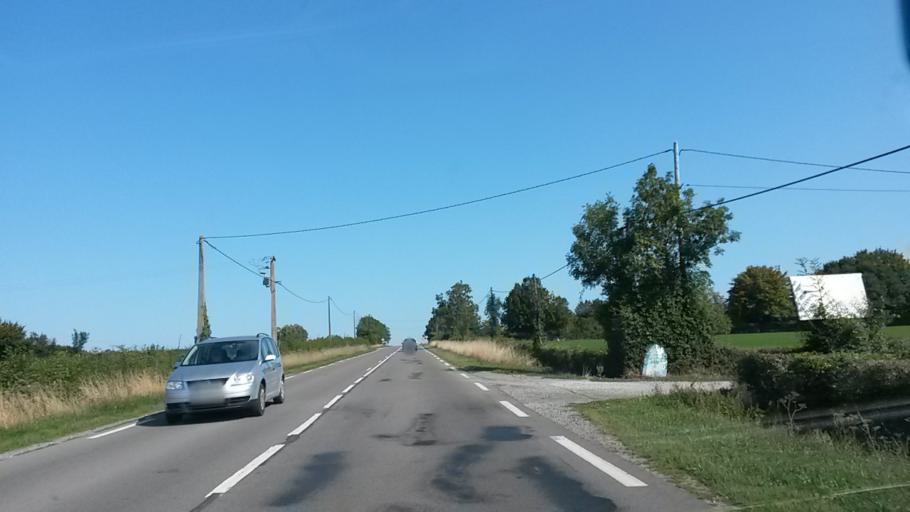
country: FR
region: Nord-Pas-de-Calais
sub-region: Departement du Nord
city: Avesnes-sur-Helpe
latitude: 50.1024
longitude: 3.9311
